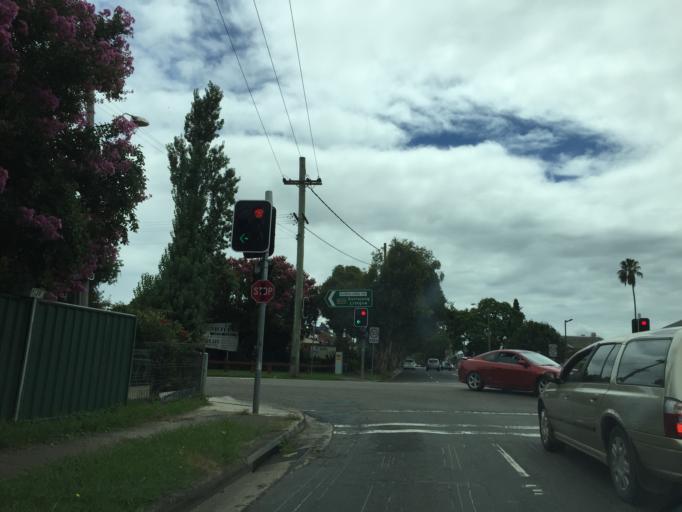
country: AU
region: New South Wales
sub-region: Hawkesbury
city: Richmond
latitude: -33.5970
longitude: 150.7468
